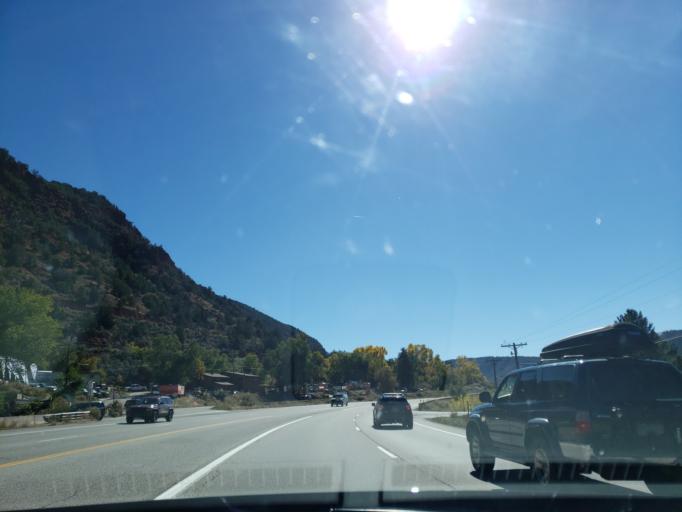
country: US
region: Colorado
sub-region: Garfield County
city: Glenwood Springs
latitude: 39.5044
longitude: -107.3018
